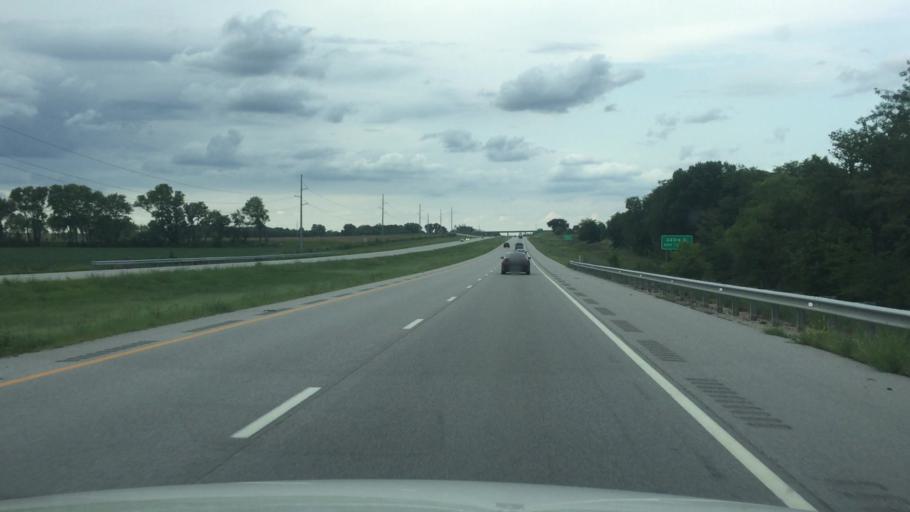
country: US
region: Kansas
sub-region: Miami County
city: Louisburg
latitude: 38.7136
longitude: -94.6763
